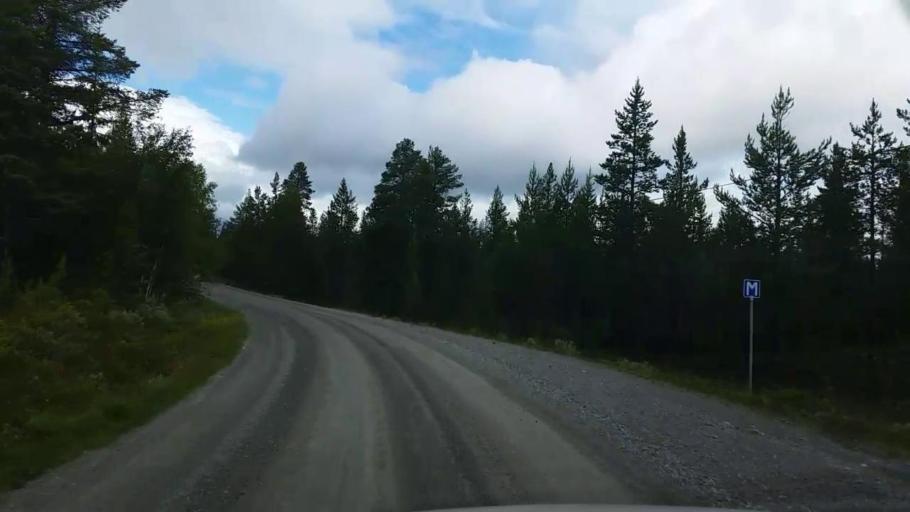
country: NO
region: Hedmark
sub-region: Engerdal
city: Engerdal
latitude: 62.3998
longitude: 12.6657
